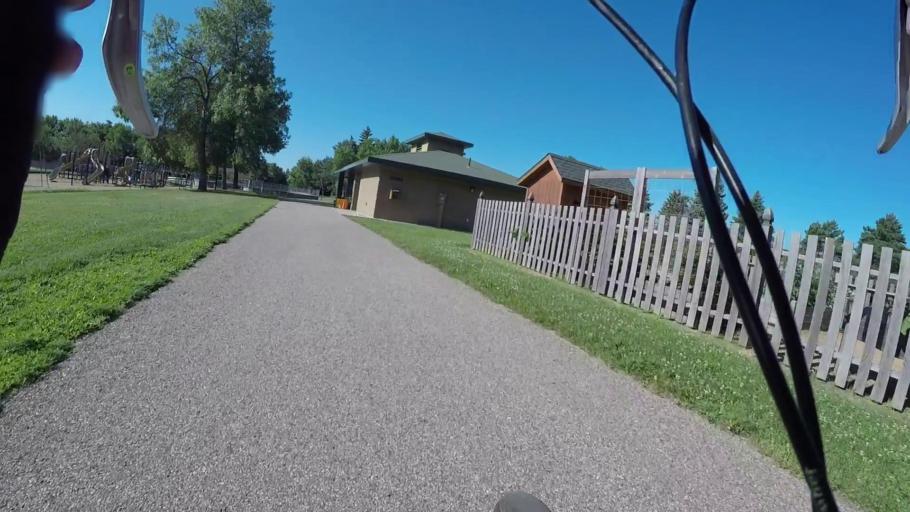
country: US
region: Minnesota
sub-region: Hennepin County
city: Eden Prairie
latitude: 44.8766
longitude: -93.4970
